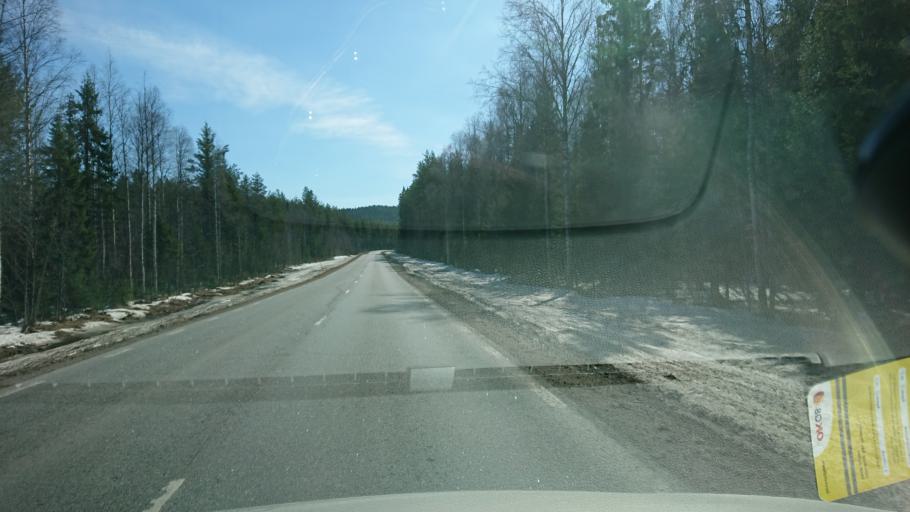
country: SE
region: Vaesternorrland
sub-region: Solleftea Kommun
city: As
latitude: 63.5715
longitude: 16.4484
